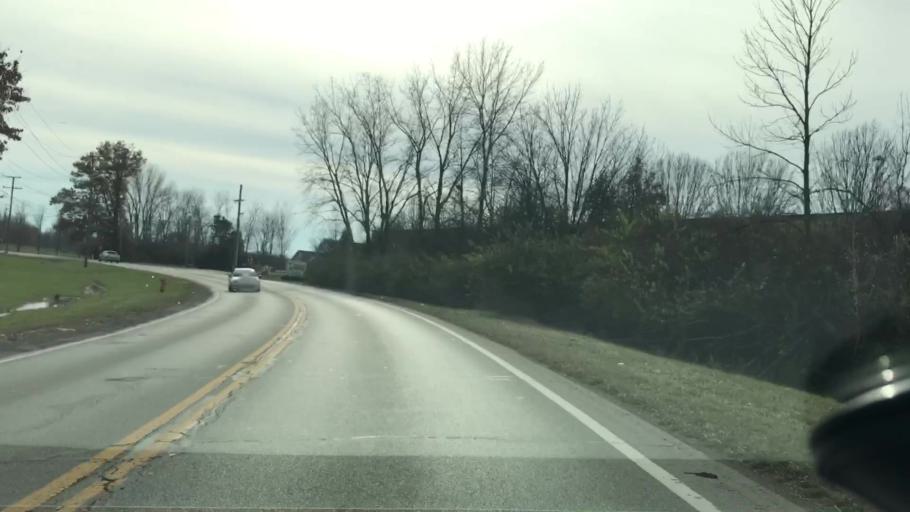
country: US
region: Ohio
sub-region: Franklin County
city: Lincoln Village
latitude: 39.9995
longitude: -83.1163
